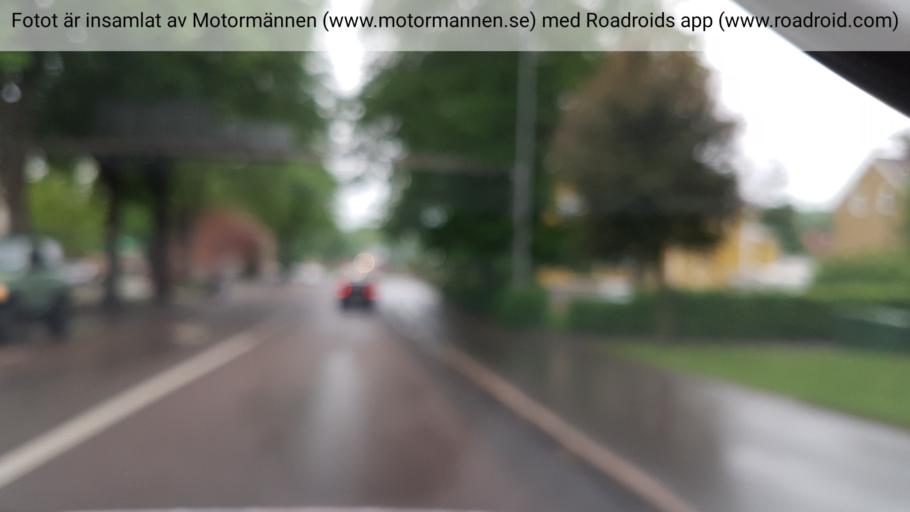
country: SE
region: Vaestra Goetaland
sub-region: Falkopings Kommun
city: Falkoeping
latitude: 58.1647
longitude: 13.5562
